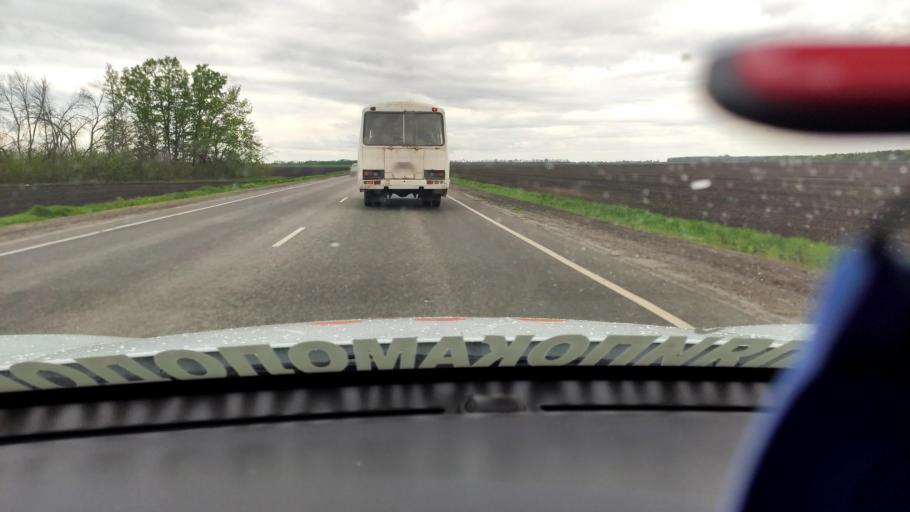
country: RU
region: Voronezj
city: Liski
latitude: 51.0346
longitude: 39.6230
